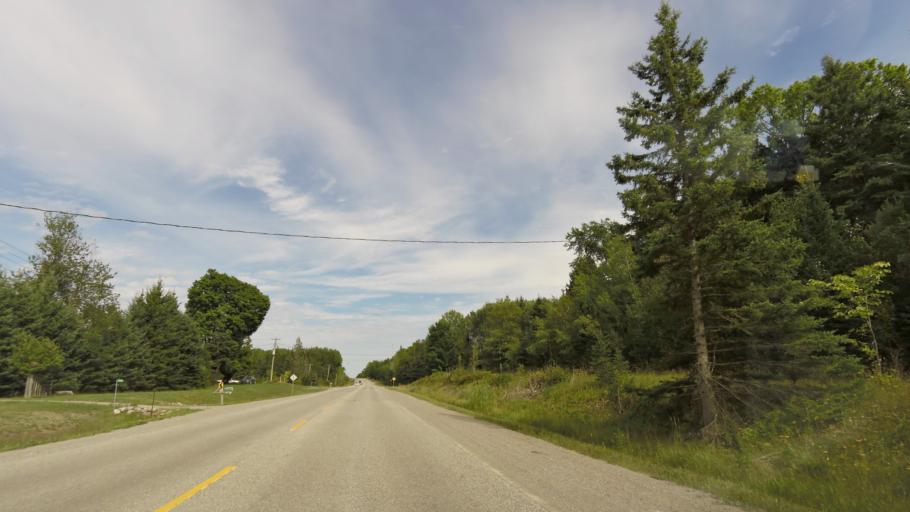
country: CA
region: Ontario
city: Omemee
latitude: 44.6568
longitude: -78.8310
